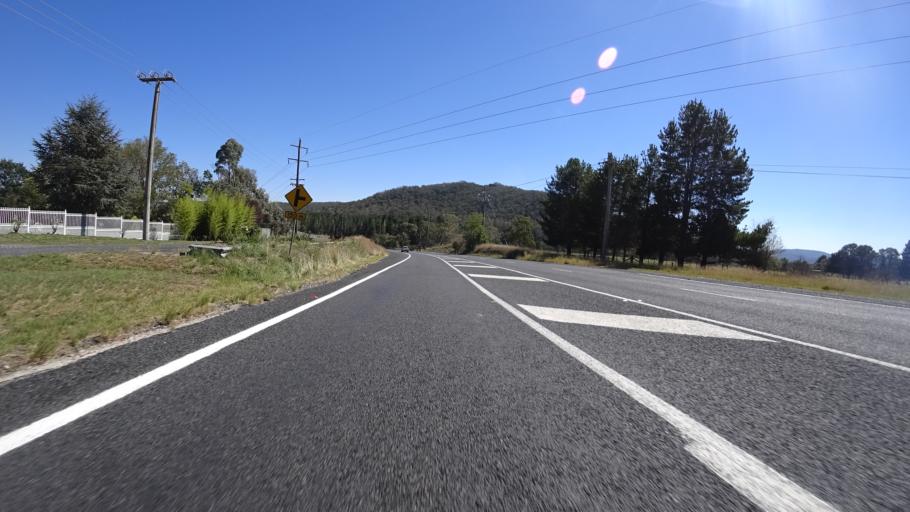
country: AU
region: New South Wales
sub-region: Lithgow
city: Portland
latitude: -33.3706
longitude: 150.0718
